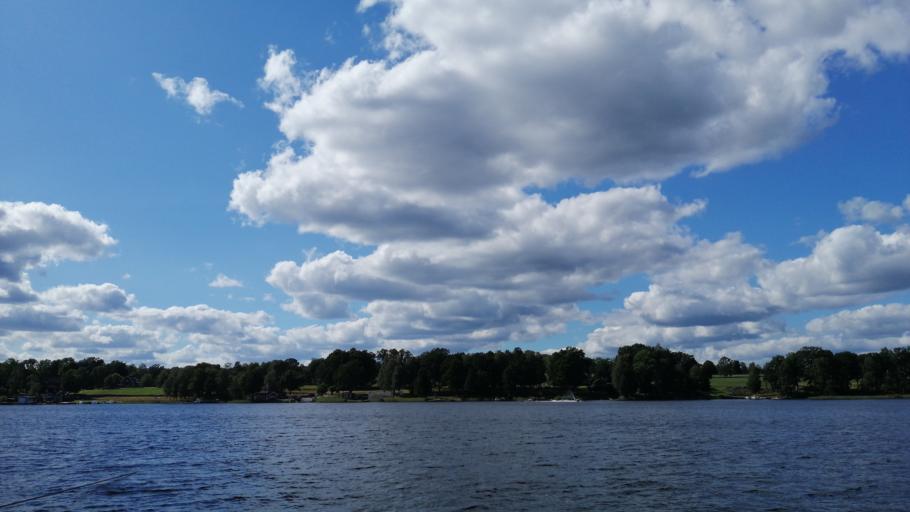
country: SE
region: Joenkoeping
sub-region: Varnamo Kommun
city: Bredaryd
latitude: 57.0085
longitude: 13.7067
